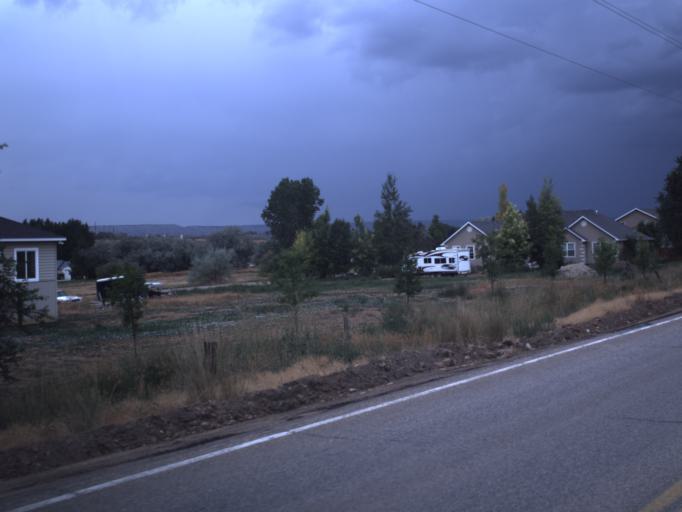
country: US
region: Utah
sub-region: Duchesne County
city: Roosevelt
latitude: 40.3295
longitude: -110.0196
